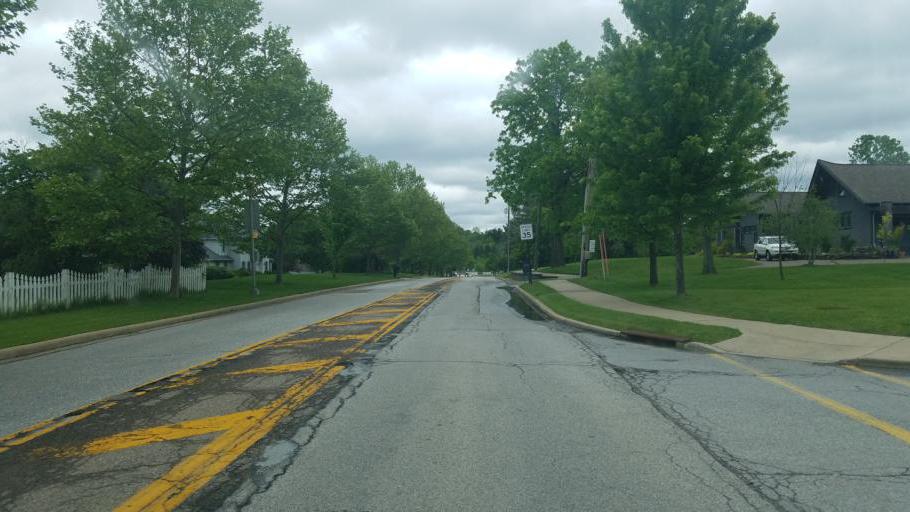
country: US
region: Ohio
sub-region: Summit County
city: Hudson
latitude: 41.2585
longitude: -81.4144
